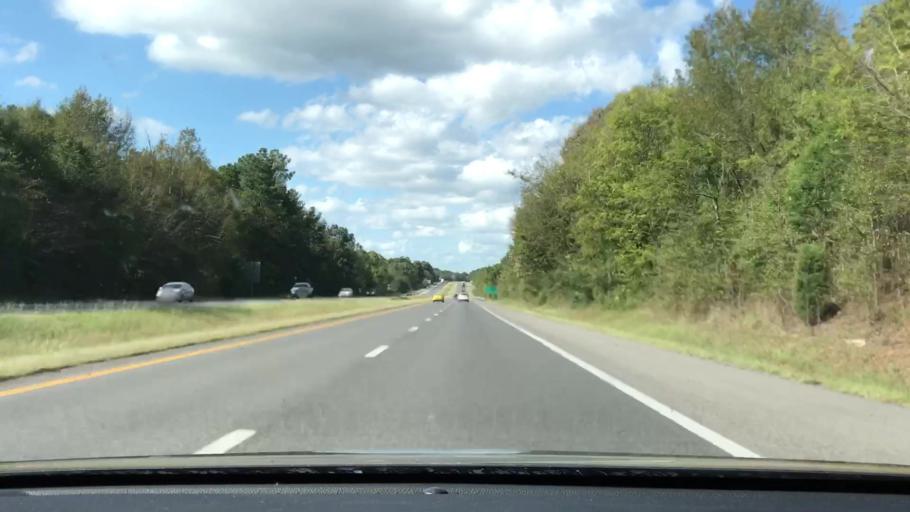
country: US
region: Kentucky
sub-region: Marshall County
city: Benton
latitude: 36.9363
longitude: -88.3435
